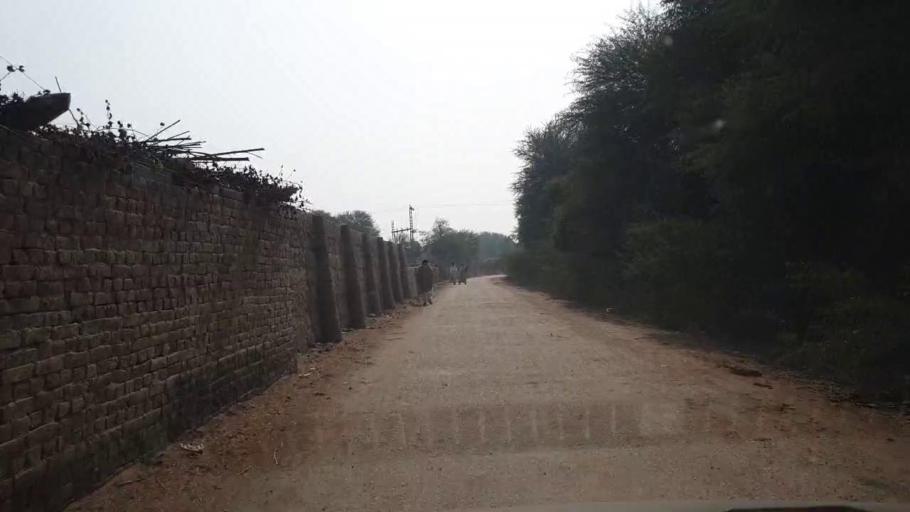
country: PK
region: Sindh
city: Bhit Shah
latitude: 25.8401
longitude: 68.4642
